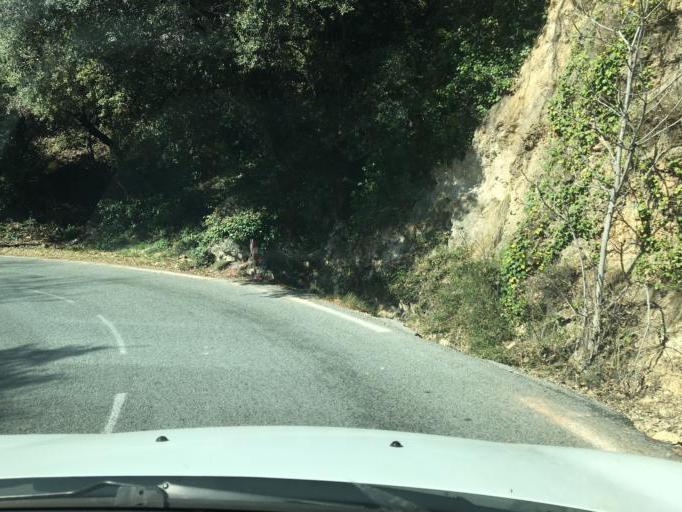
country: FR
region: Provence-Alpes-Cote d'Azur
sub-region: Departement du Var
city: Callas
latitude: 43.5966
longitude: 6.5413
